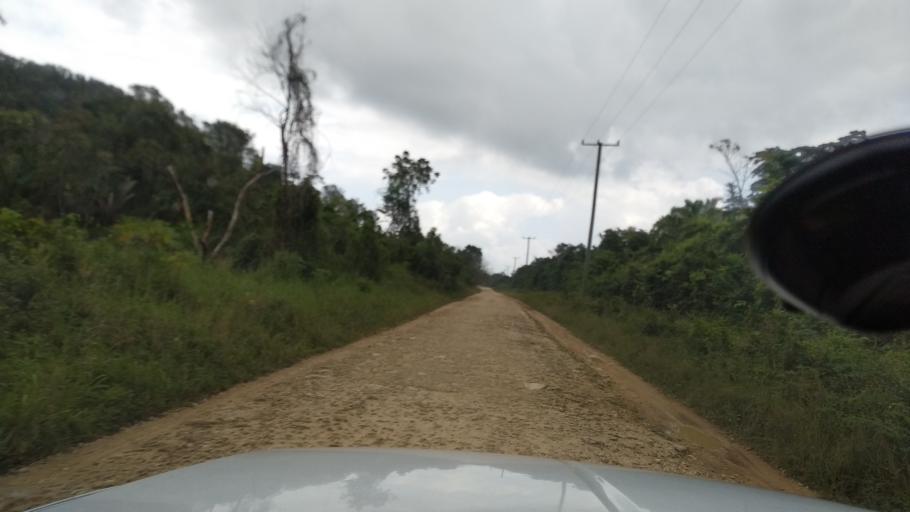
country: BZ
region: Toledo
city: Punta Gorda
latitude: 16.2142
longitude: -89.0124
